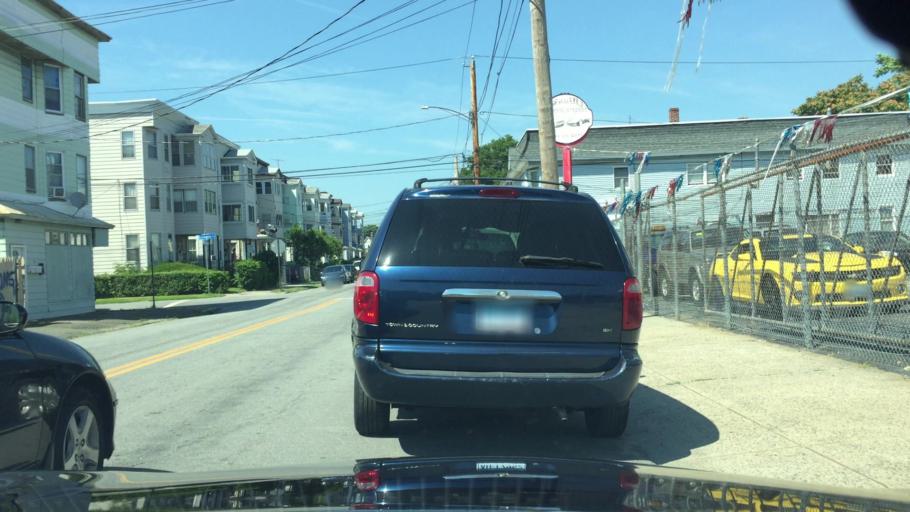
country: US
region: Connecticut
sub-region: Fairfield County
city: Bridgeport
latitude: 41.1847
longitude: -73.2016
